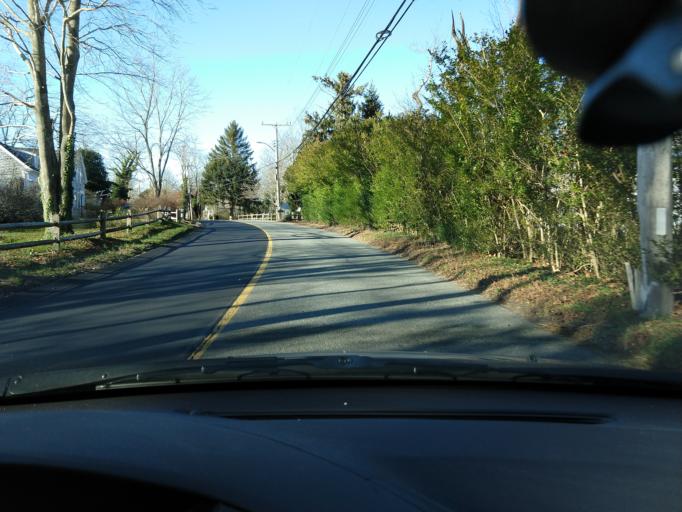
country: US
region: Massachusetts
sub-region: Barnstable County
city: Orleans
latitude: 41.7980
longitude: -69.9900
